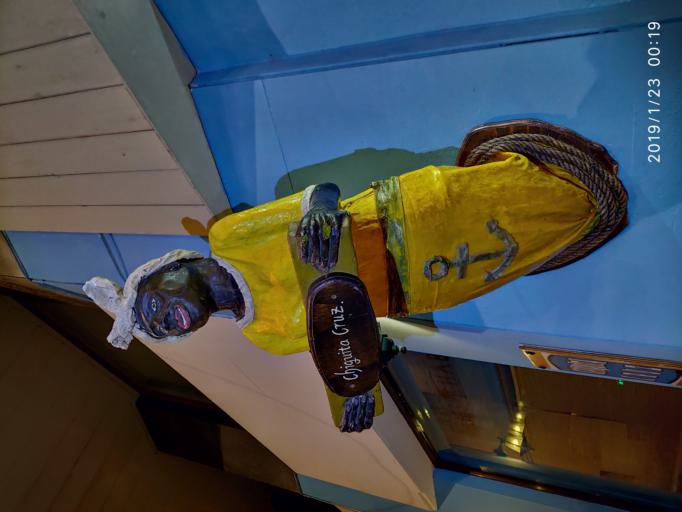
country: ES
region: Andalusia
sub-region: Provincia de Malaga
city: Malaga
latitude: 36.7203
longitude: -4.4224
